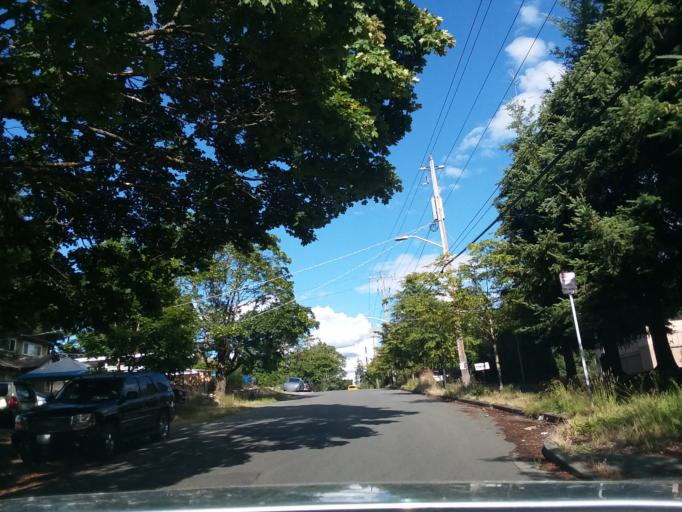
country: US
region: Washington
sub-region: King County
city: Shoreline
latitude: 47.7287
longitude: -122.3423
